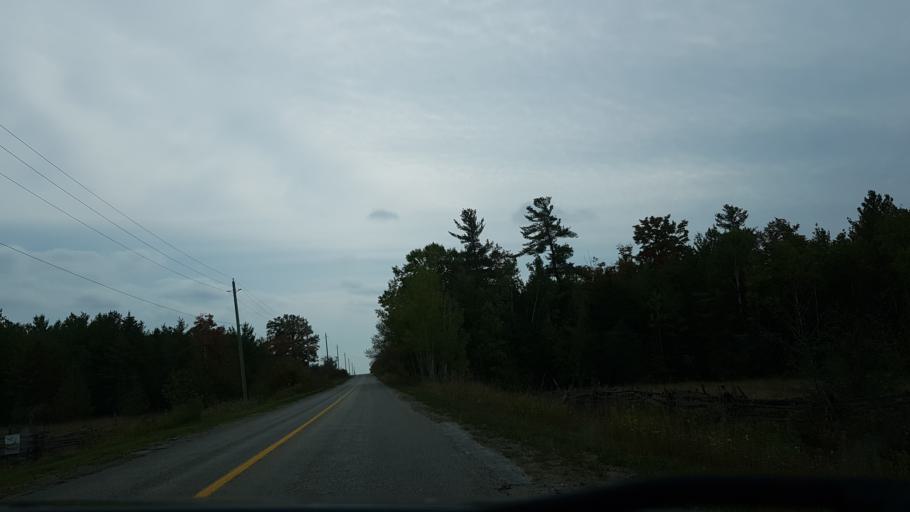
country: CA
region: Ontario
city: Orillia
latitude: 44.6904
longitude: -78.9841
